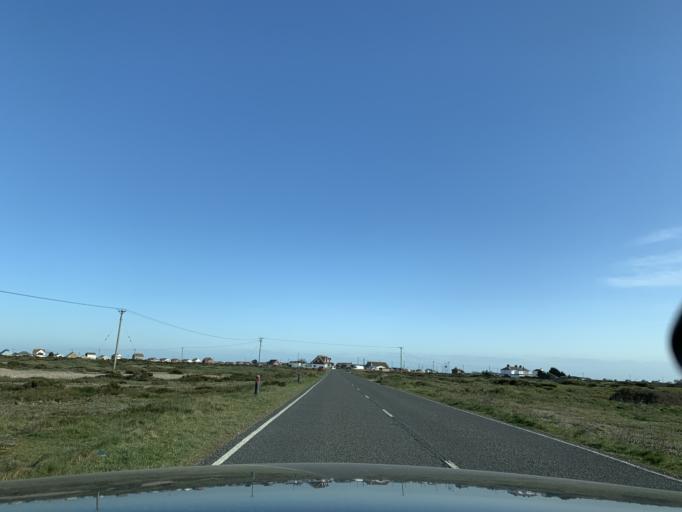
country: GB
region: England
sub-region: Kent
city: New Romney
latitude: 50.9310
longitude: 0.9652
